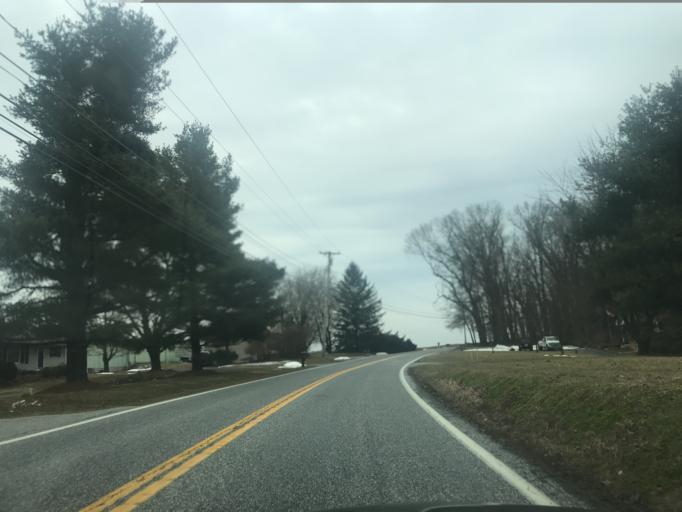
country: US
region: Maryland
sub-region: Harford County
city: Jarrettsville
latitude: 39.6594
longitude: -76.5442
